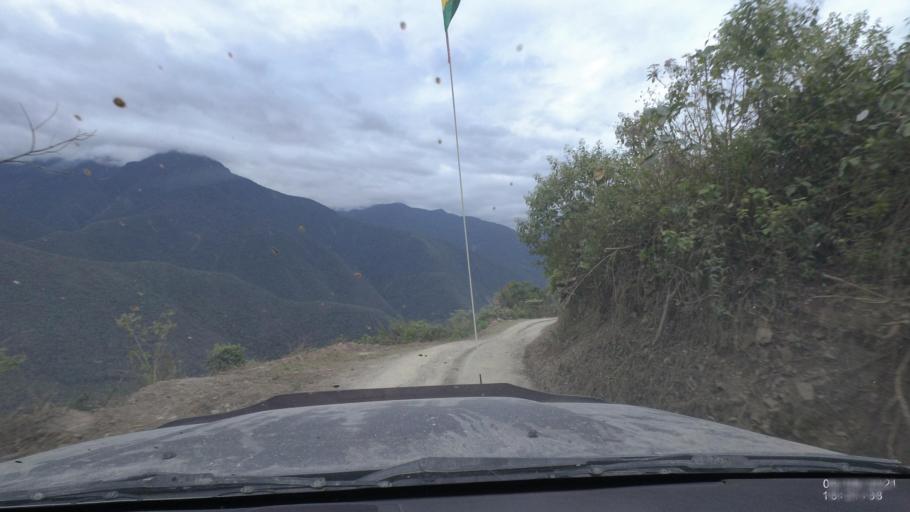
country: BO
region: La Paz
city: Quime
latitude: -16.5446
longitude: -66.7504
